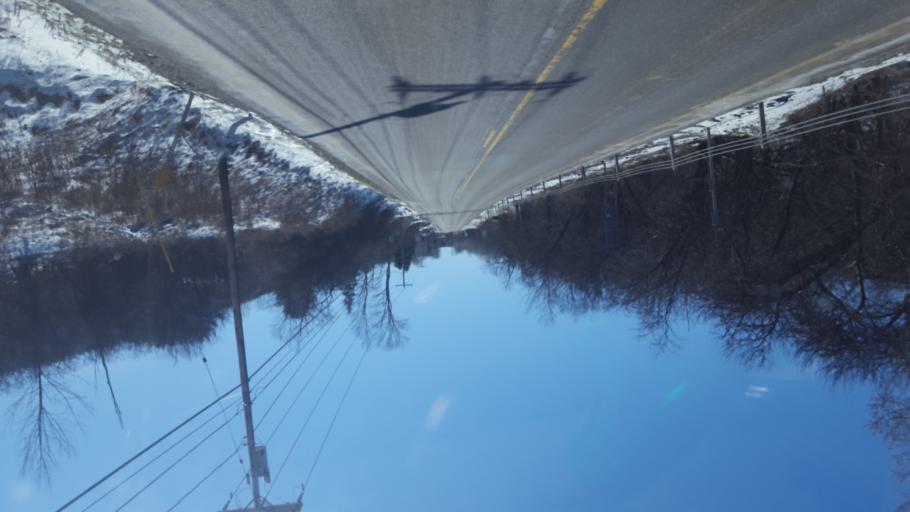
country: US
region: New York
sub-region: Allegany County
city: Andover
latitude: 42.0743
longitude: -77.8505
